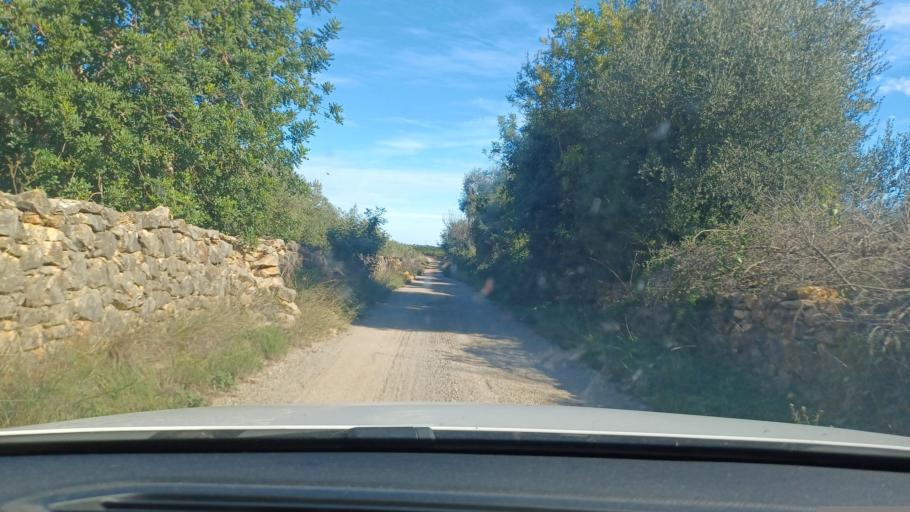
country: ES
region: Catalonia
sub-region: Provincia de Tarragona
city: Santa Barbara
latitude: 40.6835
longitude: 0.4961
